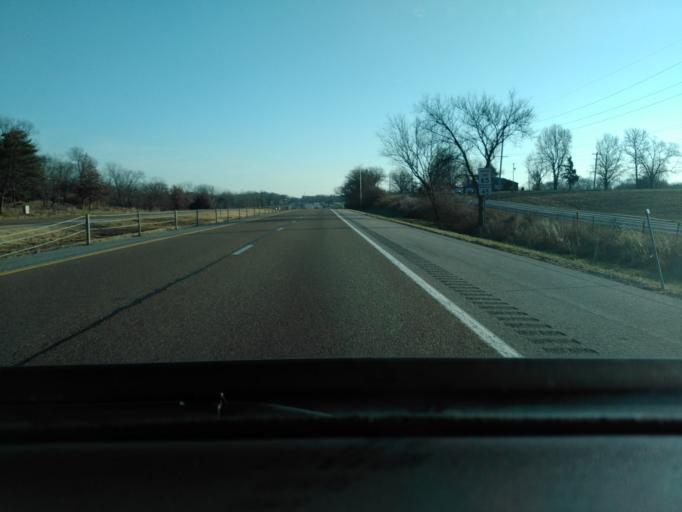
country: US
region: Illinois
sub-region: Madison County
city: Maryville
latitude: 38.7094
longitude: -89.9495
